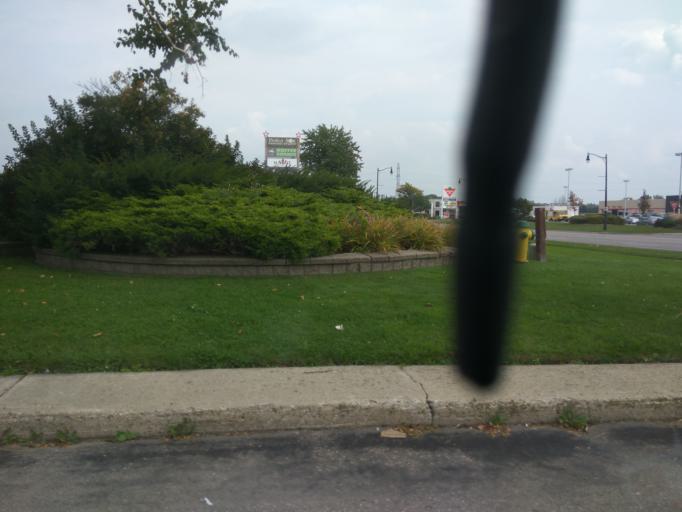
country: CA
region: Ontario
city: Stratford
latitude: 43.3710
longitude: -80.9454
